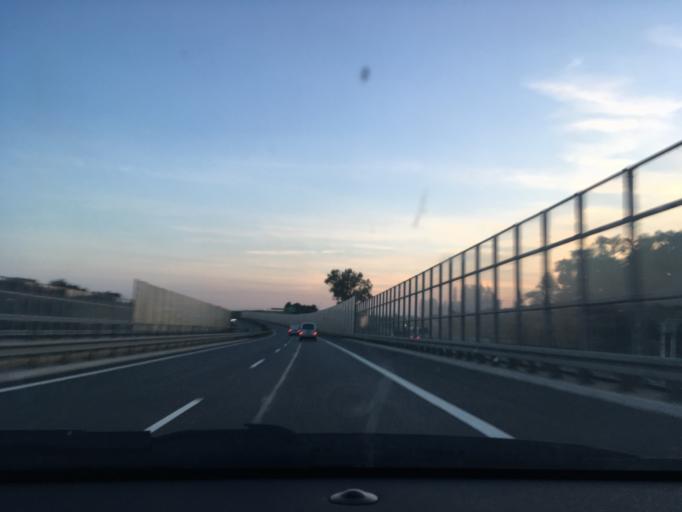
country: PL
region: Podlasie
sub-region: Powiat zambrowski
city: Zambrow
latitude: 52.9914
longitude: 22.2263
